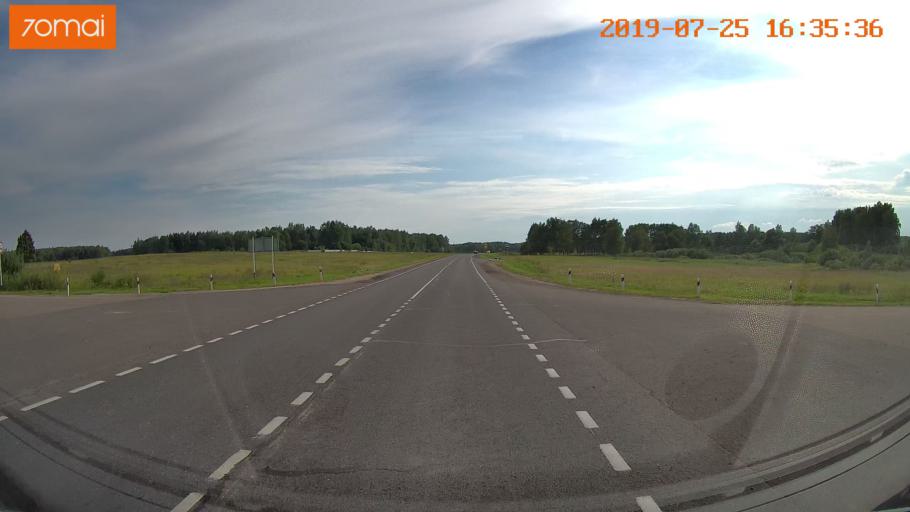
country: RU
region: Ivanovo
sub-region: Privolzhskiy Rayon
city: Ples
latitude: 57.4036
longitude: 41.4188
